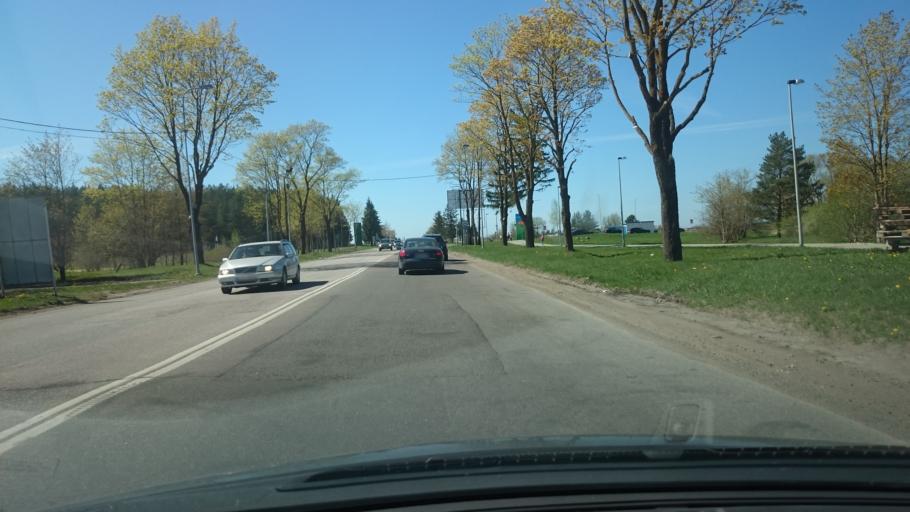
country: EE
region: Ida-Virumaa
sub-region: Narva linn
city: Narva
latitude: 59.3847
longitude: 28.1571
